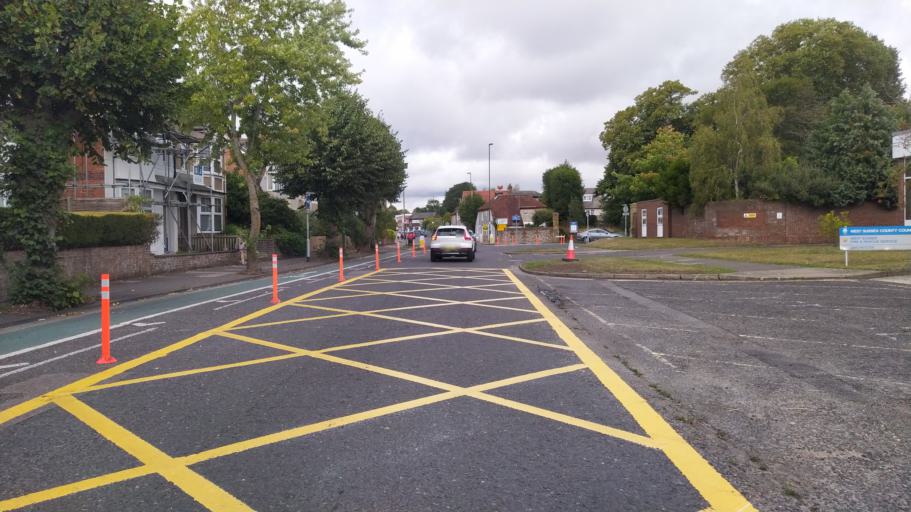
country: GB
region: England
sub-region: West Sussex
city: Chichester
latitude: 50.8405
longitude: -0.7800
